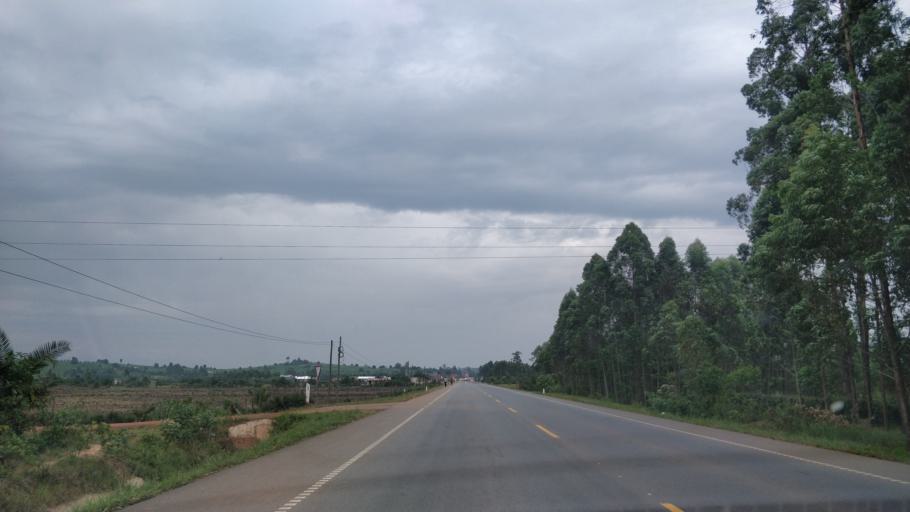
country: UG
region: Western Region
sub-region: Sheema District
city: Kibingo
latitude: -0.6661
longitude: 30.4473
